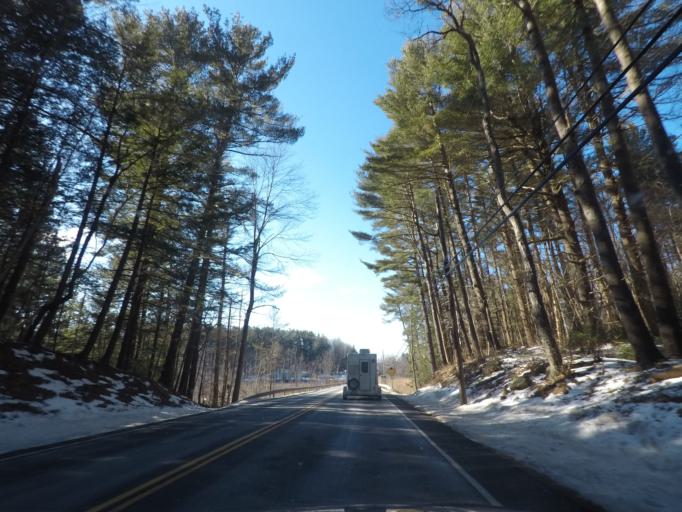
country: US
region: Massachusetts
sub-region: Berkshire County
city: Richmond
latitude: 42.4101
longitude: -73.4393
